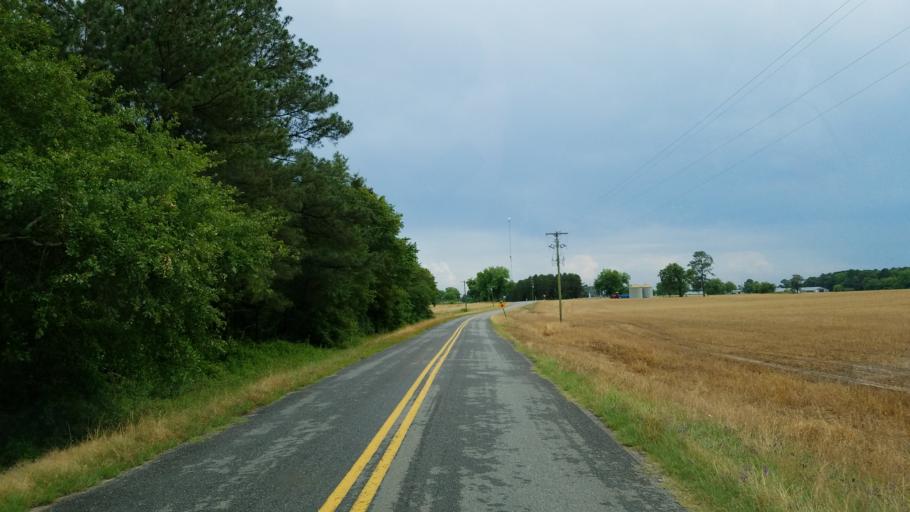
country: US
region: Georgia
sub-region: Dooly County
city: Unadilla
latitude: 32.2496
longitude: -83.7973
